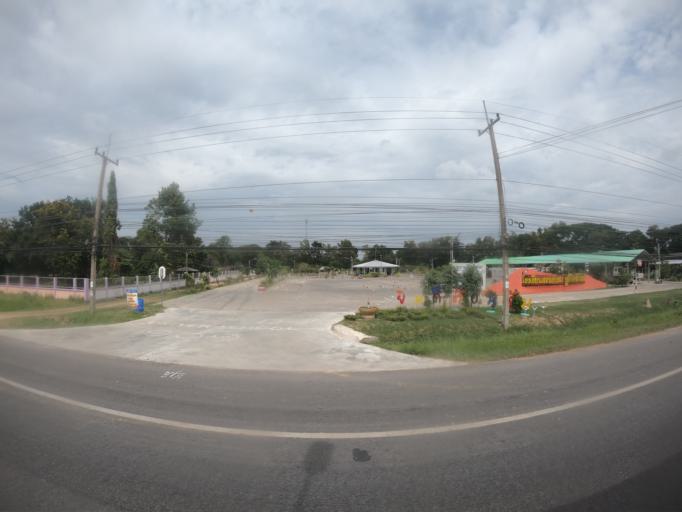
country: TH
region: Roi Et
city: Roi Et
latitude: 16.0695
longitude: 103.6042
